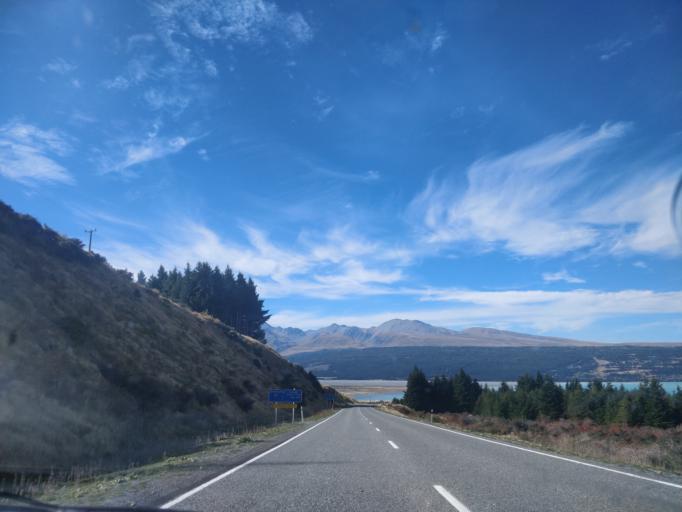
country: NZ
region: Canterbury
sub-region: Timaru District
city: Pleasant Point
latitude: -43.9145
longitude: 170.1154
